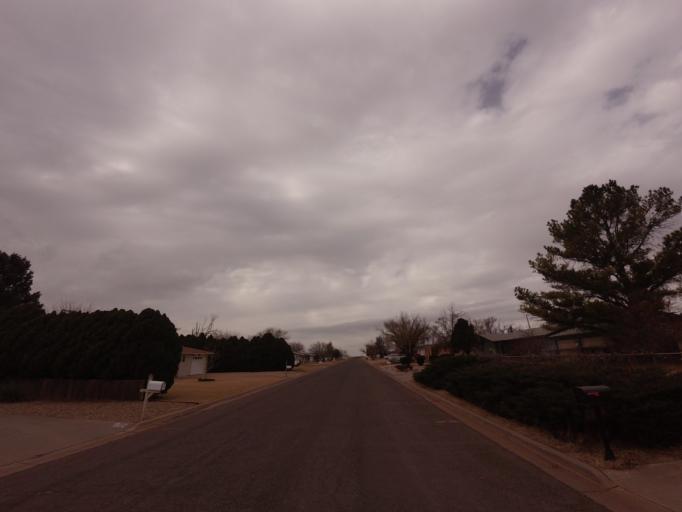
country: US
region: New Mexico
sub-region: Curry County
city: Clovis
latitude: 34.3824
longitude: -103.2011
